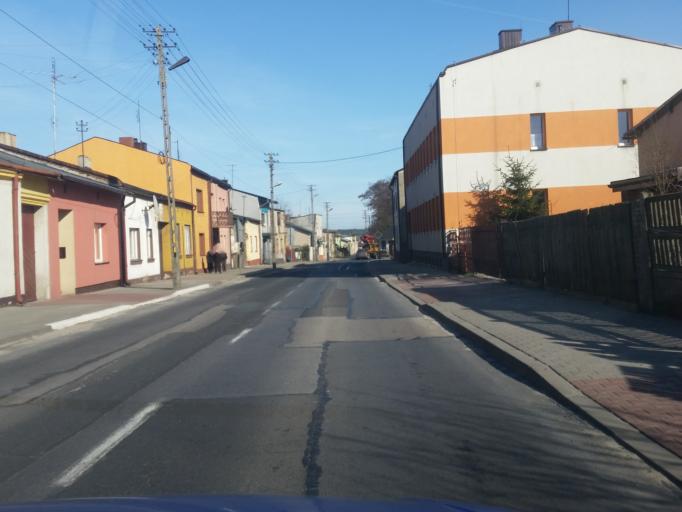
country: PL
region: Lodz Voivodeship
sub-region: Powiat radomszczanski
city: Kamiensk
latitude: 51.2051
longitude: 19.4967
